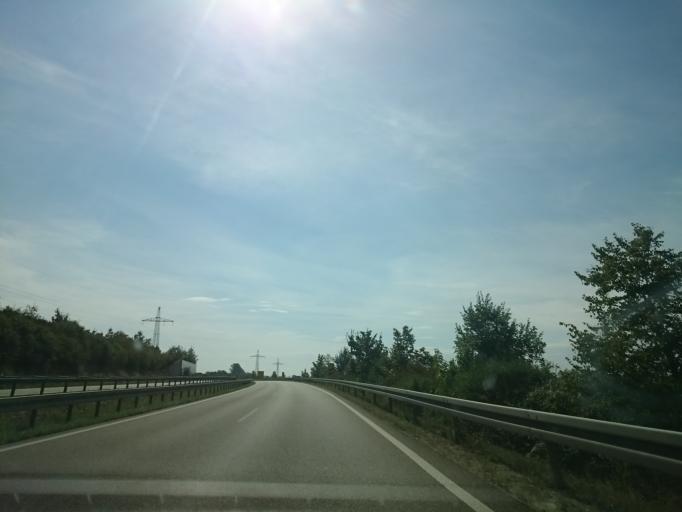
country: DE
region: Bavaria
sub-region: Swabia
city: Biberbach
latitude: 48.5279
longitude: 10.8311
